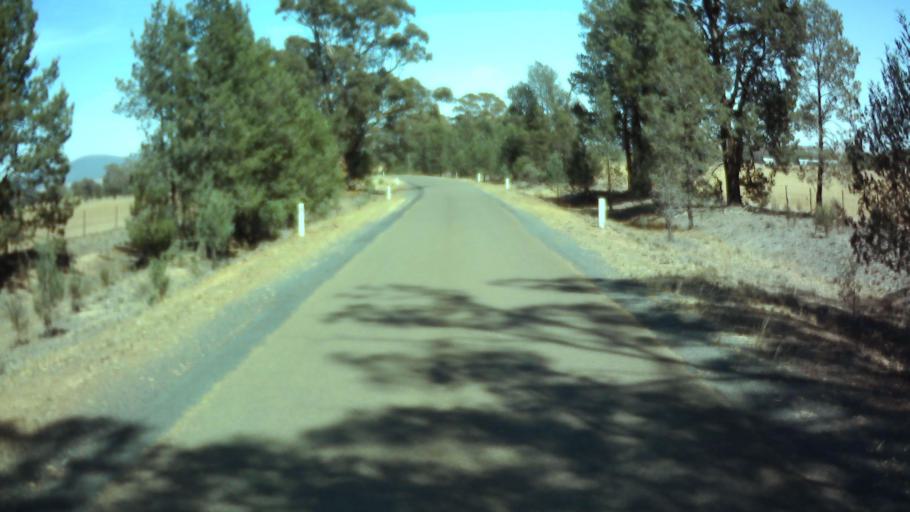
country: AU
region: New South Wales
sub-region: Weddin
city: Grenfell
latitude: -33.8699
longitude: 148.1093
